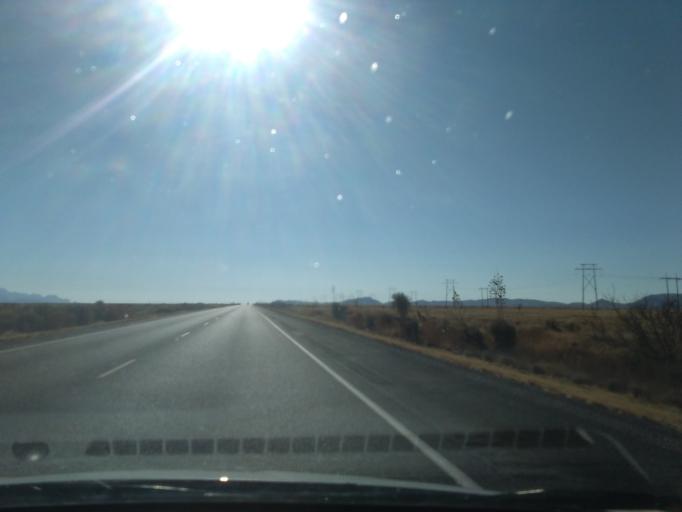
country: US
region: New Mexico
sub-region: Luna County
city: Deming
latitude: 32.4710
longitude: -107.5355
